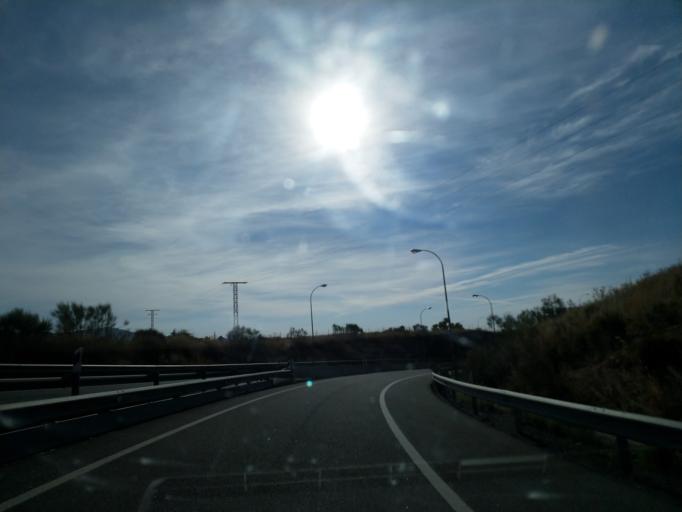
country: ES
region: Castille and Leon
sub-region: Provincia de Segovia
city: Villacastin
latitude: 40.7718
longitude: -4.4205
